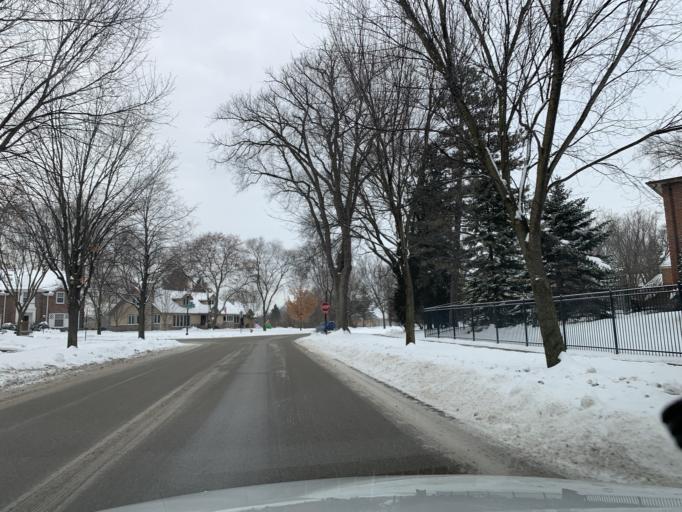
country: US
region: Minnesota
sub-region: Hennepin County
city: Edina
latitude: 44.9145
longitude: -93.3412
